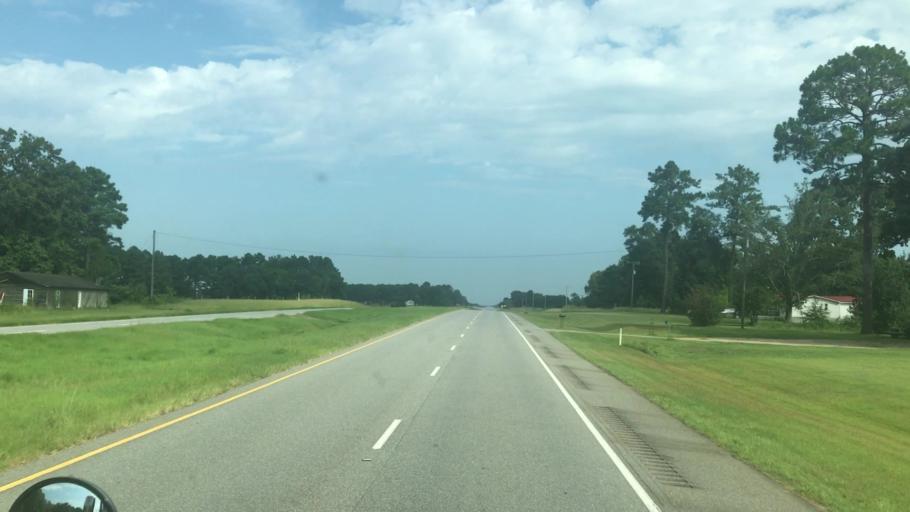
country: US
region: Georgia
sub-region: Early County
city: Blakely
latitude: 31.3120
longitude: -84.8727
